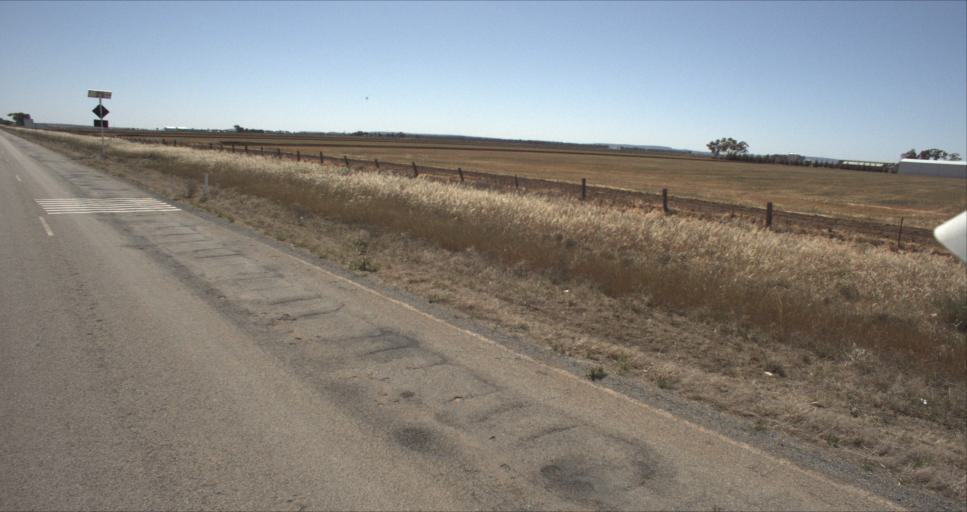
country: AU
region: New South Wales
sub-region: Leeton
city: Leeton
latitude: -34.5185
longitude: 146.2837
